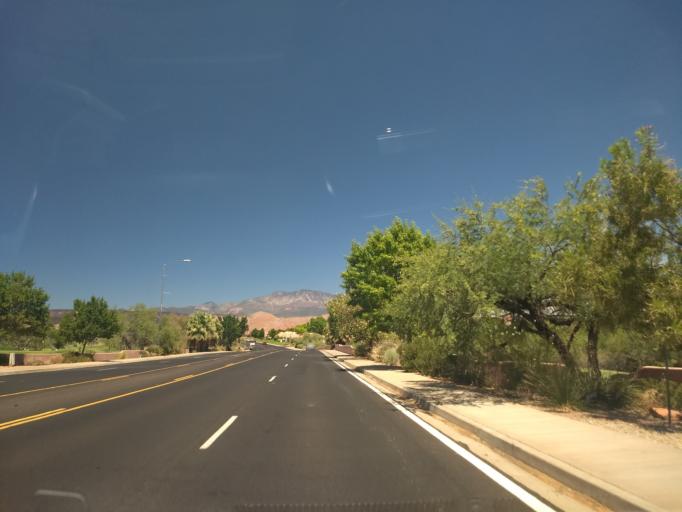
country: US
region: Utah
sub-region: Washington County
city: Washington
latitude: 37.1336
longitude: -113.5265
